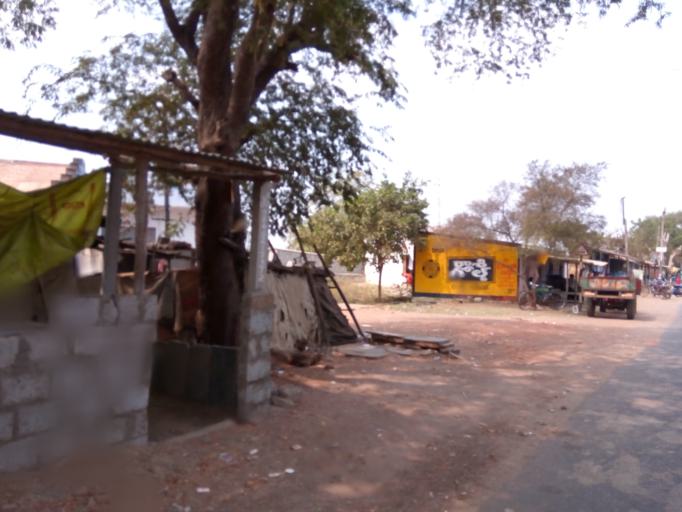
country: IN
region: Andhra Pradesh
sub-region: Prakasam
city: pedda nakkalapalem
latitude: 15.9629
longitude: 80.2789
